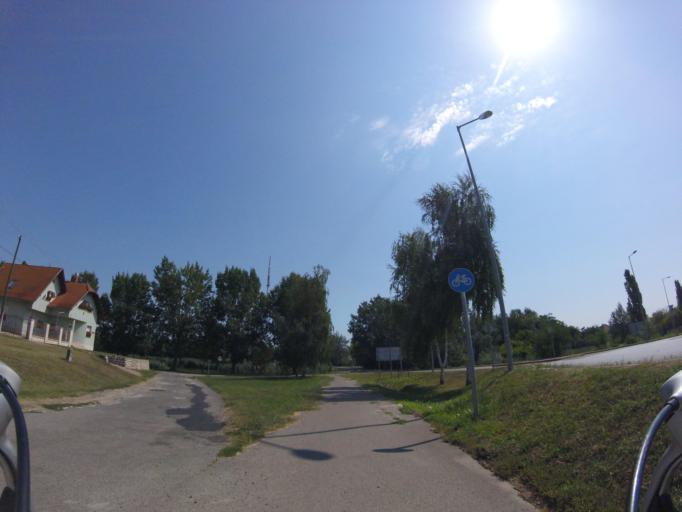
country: HU
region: Bacs-Kiskun
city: Csavoly
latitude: 46.1960
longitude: 19.1446
